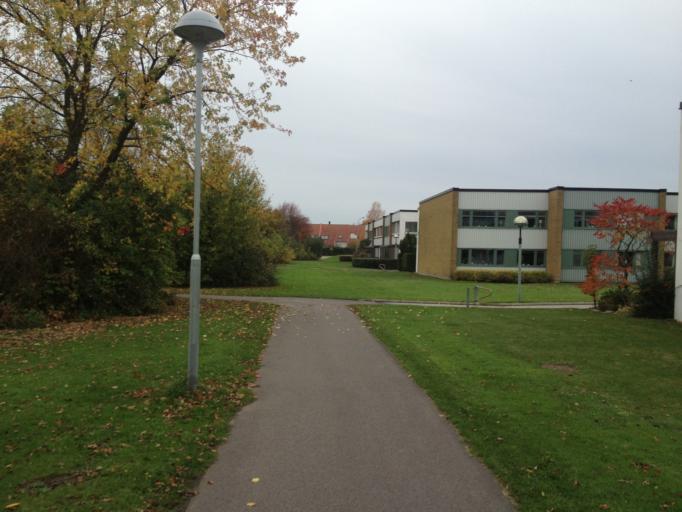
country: SE
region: Skane
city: Bjarred
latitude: 55.7195
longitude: 13.0205
